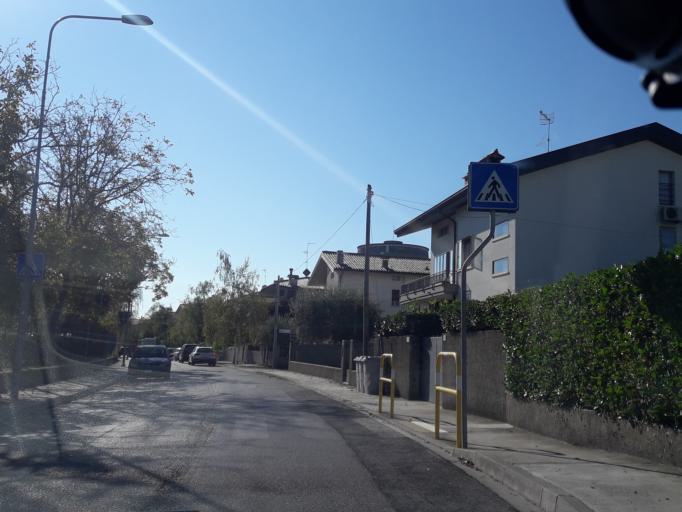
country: IT
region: Friuli Venezia Giulia
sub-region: Provincia di Udine
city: Udine
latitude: 46.0873
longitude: 13.2419
